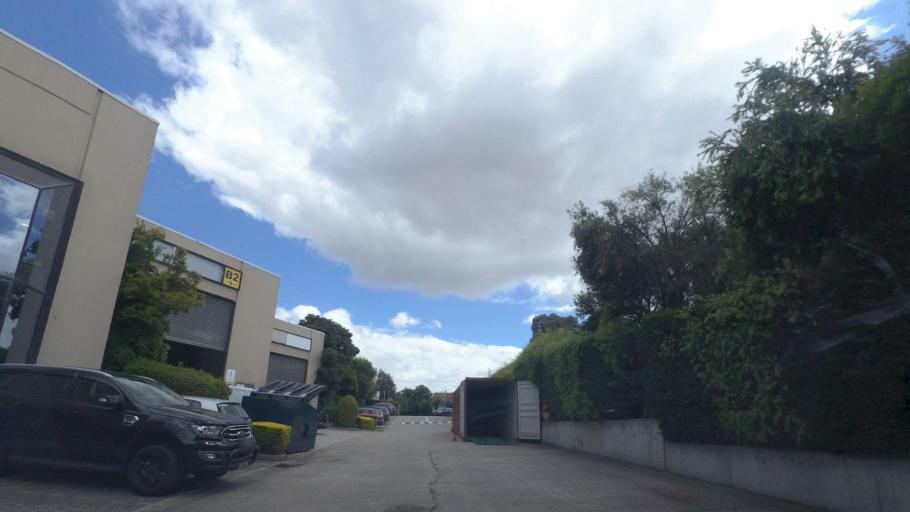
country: AU
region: Victoria
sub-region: Knox
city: Scoresby
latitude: -37.9014
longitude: 145.2311
